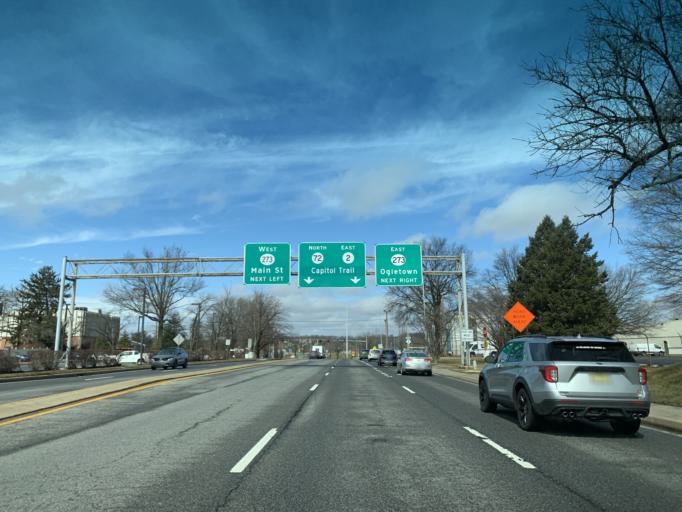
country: US
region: Delaware
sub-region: New Castle County
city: Newark
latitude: 39.6830
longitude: -75.7364
